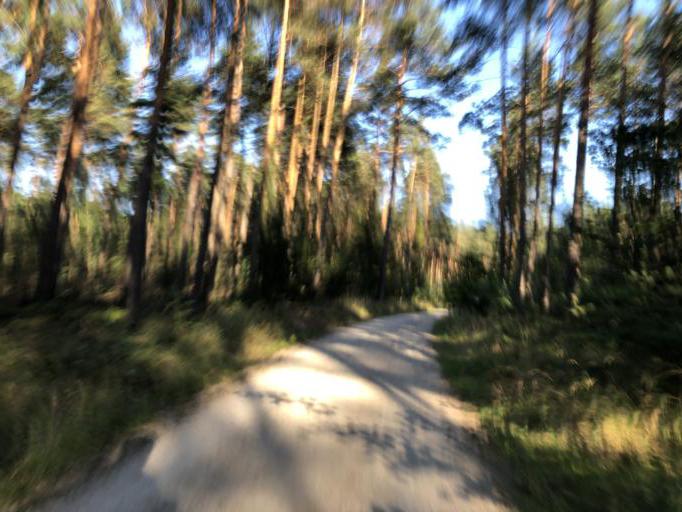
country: DE
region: Bavaria
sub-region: Regierungsbezirk Mittelfranken
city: Uttenreuth
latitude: 49.5527
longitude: 11.0821
